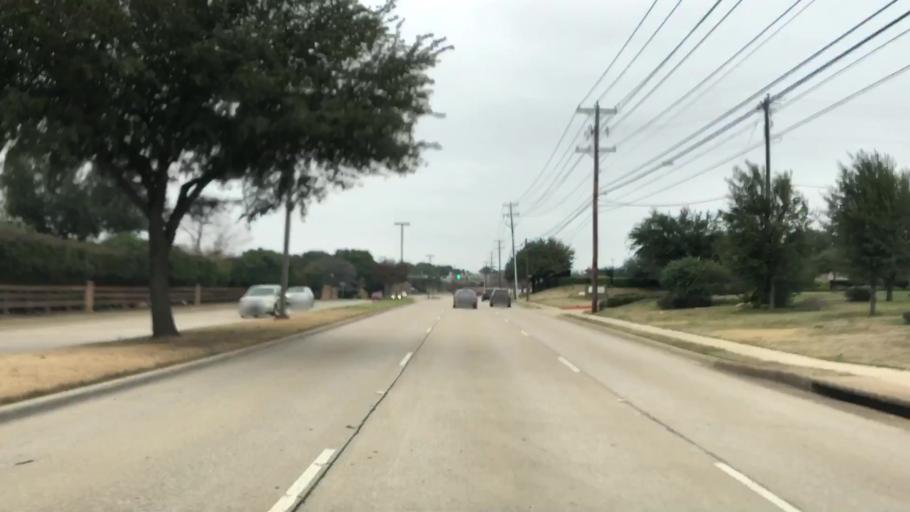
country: US
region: Texas
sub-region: Dallas County
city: Addison
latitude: 32.9783
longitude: -96.8555
